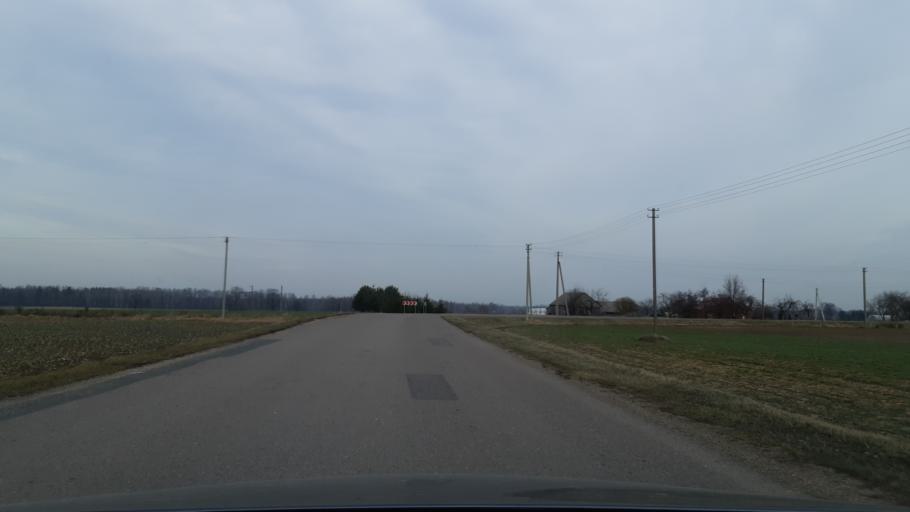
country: LT
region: Marijampoles apskritis
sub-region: Marijampole Municipality
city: Marijampole
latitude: 54.7174
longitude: 23.3226
